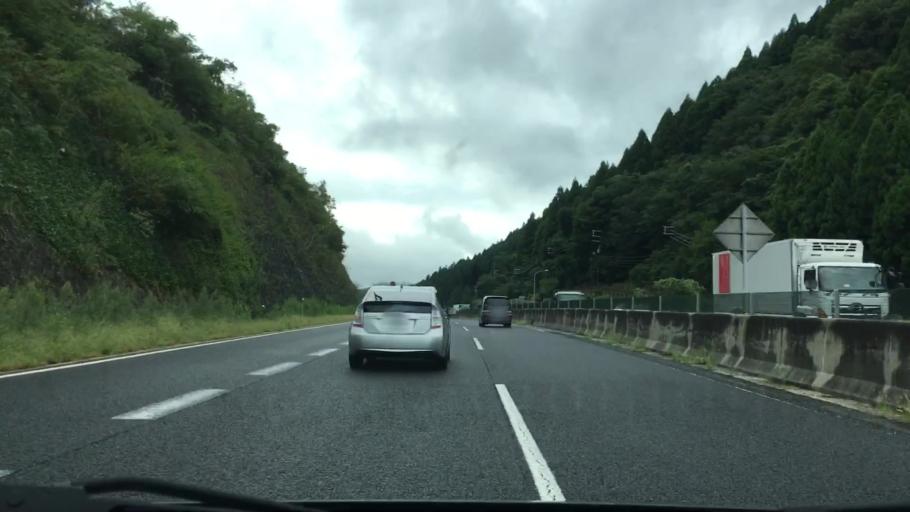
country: JP
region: Hyogo
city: Yamazakicho-nakabirose
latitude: 35.0413
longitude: 134.4687
